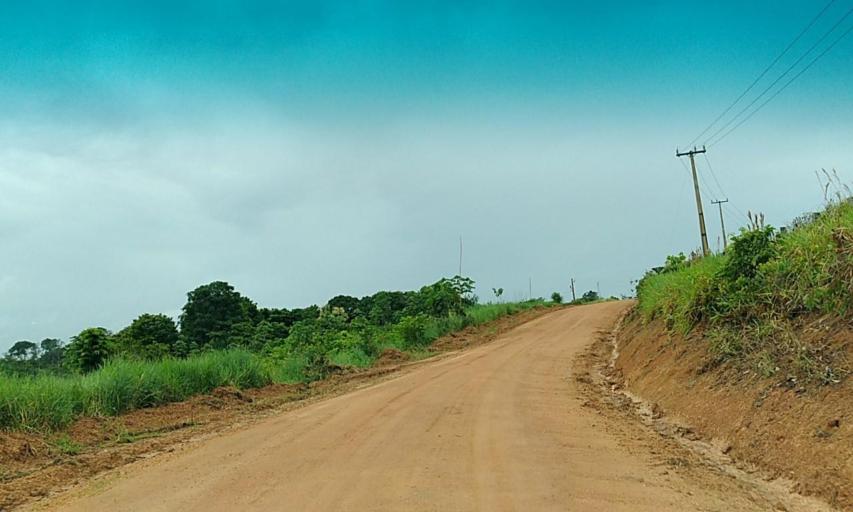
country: BR
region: Para
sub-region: Senador Jose Porfirio
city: Senador Jose Porfirio
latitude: -3.0601
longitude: -51.6615
